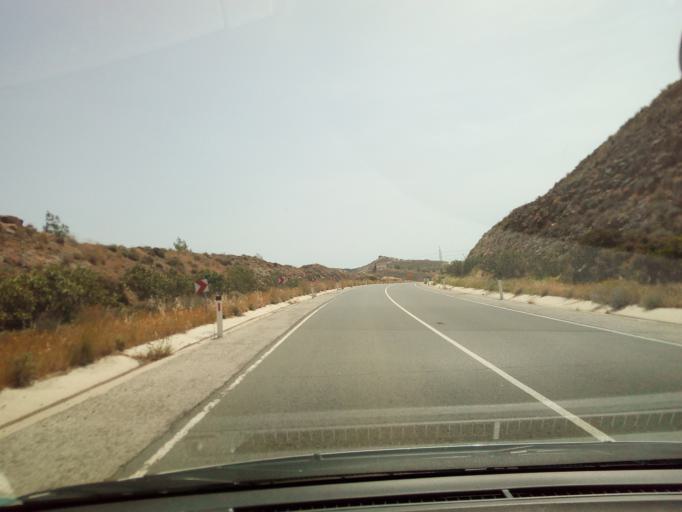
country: CY
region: Larnaka
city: Troulloi
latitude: 35.0013
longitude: 33.5716
